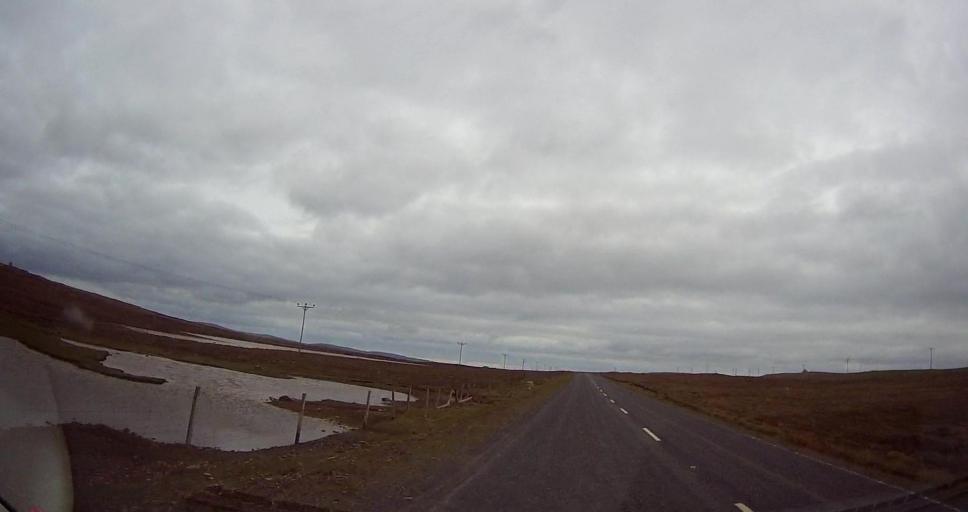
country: GB
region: Scotland
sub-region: Shetland Islands
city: Shetland
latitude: 60.7162
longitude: -0.9137
